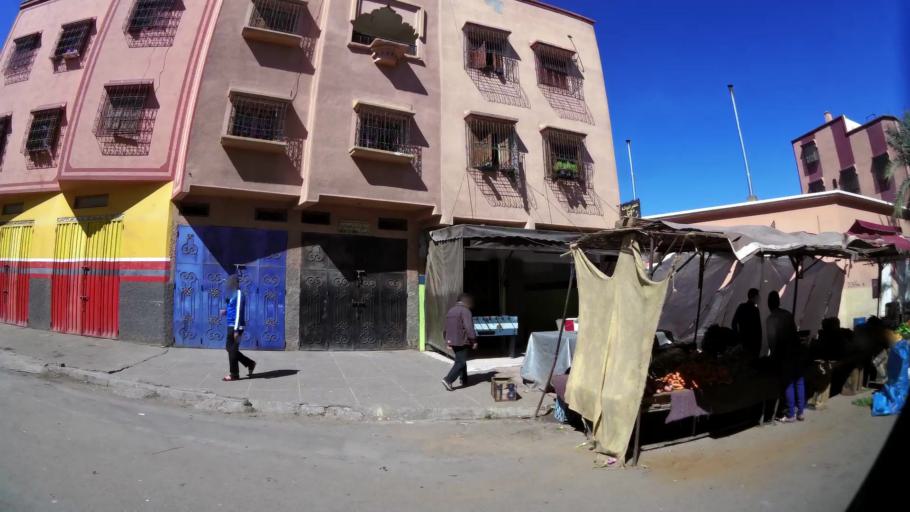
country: MA
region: Marrakech-Tensift-Al Haouz
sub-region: Marrakech
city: Marrakesh
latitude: 31.6460
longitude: -7.9825
